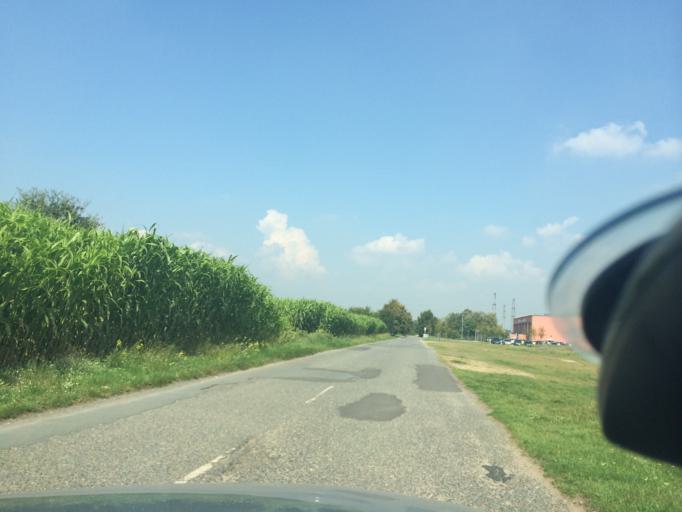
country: DE
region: Hesse
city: Morfelden-Walldorf
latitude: 49.9875
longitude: 8.5624
